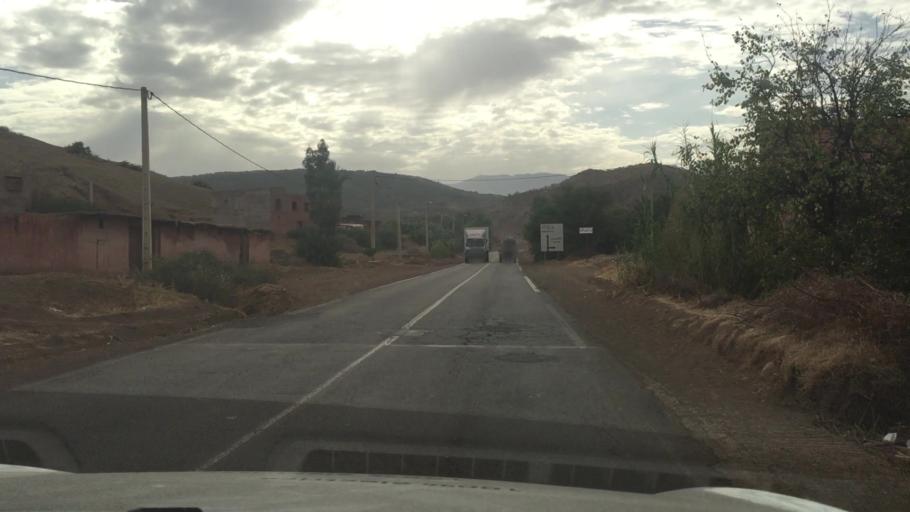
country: MA
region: Marrakech-Tensift-Al Haouz
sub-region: Al-Haouz
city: Touama
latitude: 31.5482
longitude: -7.5754
